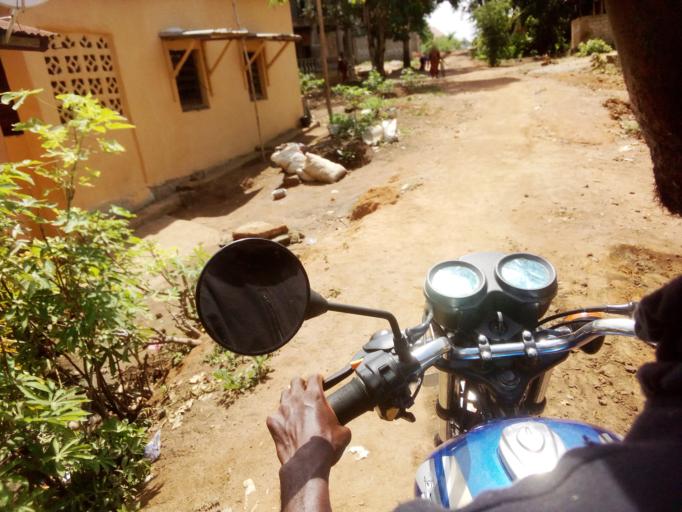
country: SL
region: Western Area
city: Waterloo
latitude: 8.3383
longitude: -13.0692
